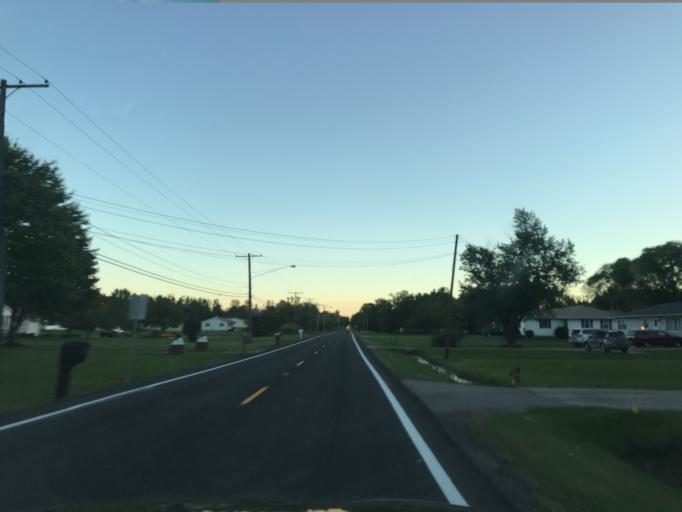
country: US
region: Ohio
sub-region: Ashtabula County
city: Ashtabula
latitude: 41.8701
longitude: -80.8574
